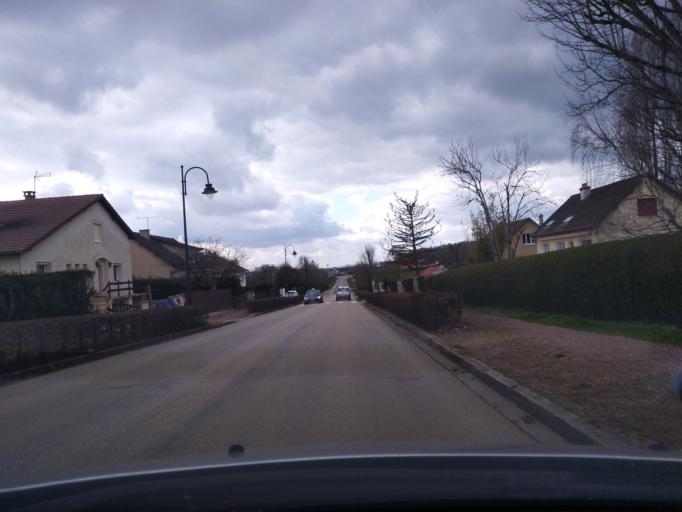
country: FR
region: Bourgogne
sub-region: Departement de l'Yonne
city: Avallon
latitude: 47.5101
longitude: 3.9391
